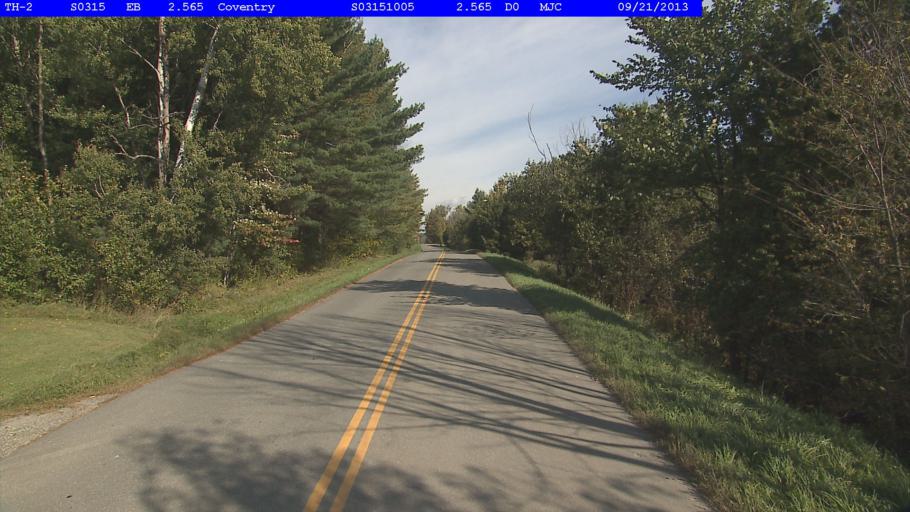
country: US
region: Vermont
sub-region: Orleans County
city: Newport
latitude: 44.8732
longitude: -72.2148
